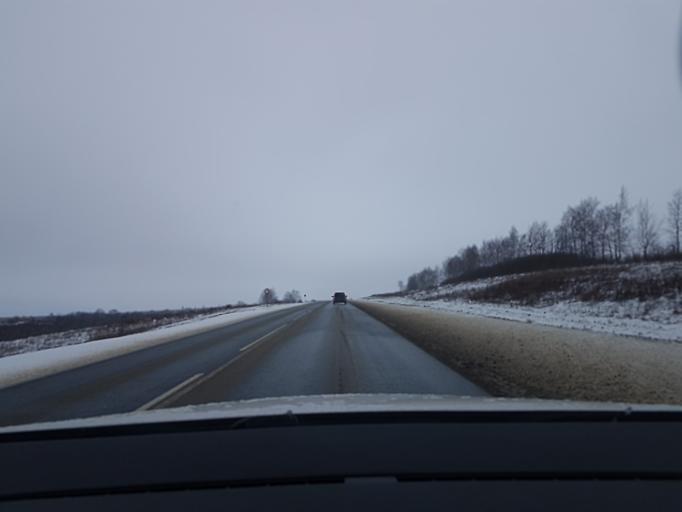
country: RU
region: Moskovskaya
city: Serebryanyye Prudy
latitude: 54.4128
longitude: 38.6518
